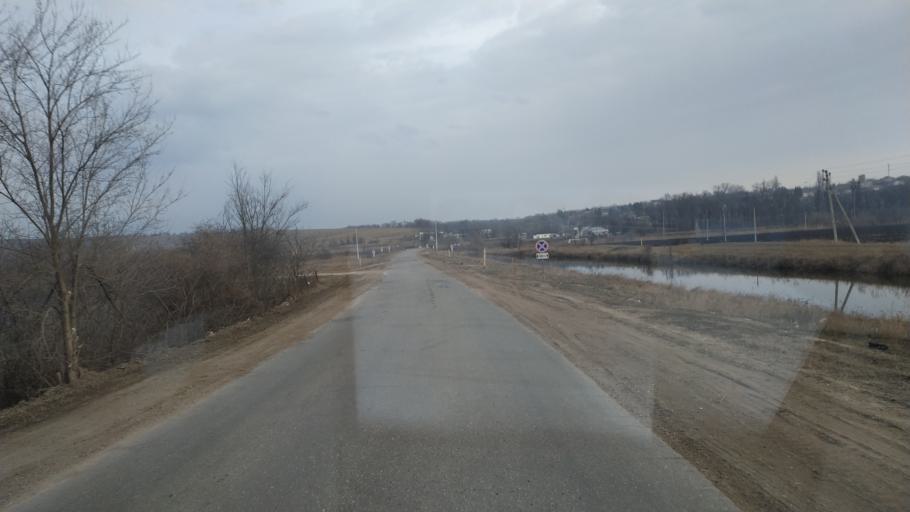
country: MD
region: Chisinau
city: Singera
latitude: 46.9206
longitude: 29.0464
